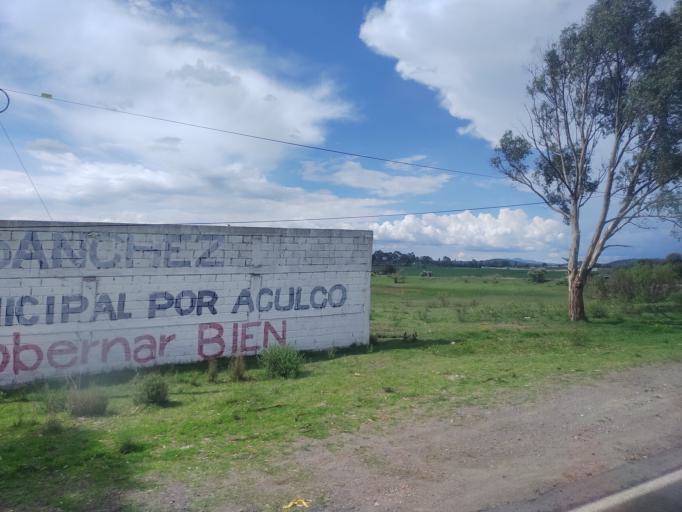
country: MX
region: Mexico
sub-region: Aculco
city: El Colorado
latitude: 20.0965
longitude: -99.7500
